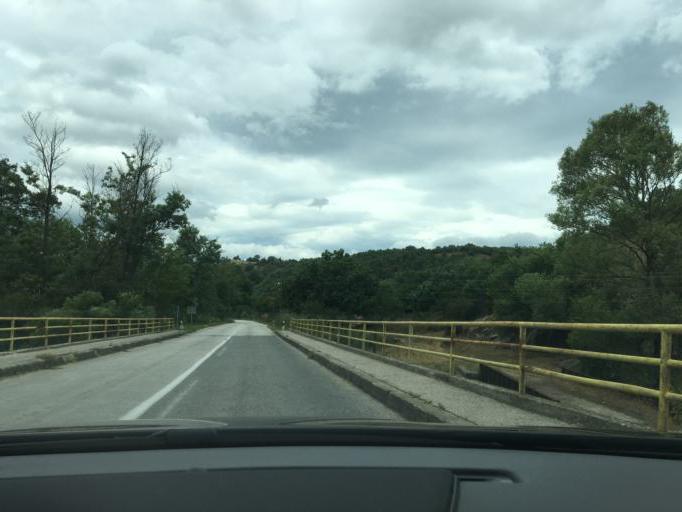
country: MK
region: Kriva Palanka
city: Kriva Palanka
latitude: 42.1763
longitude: 22.2463
